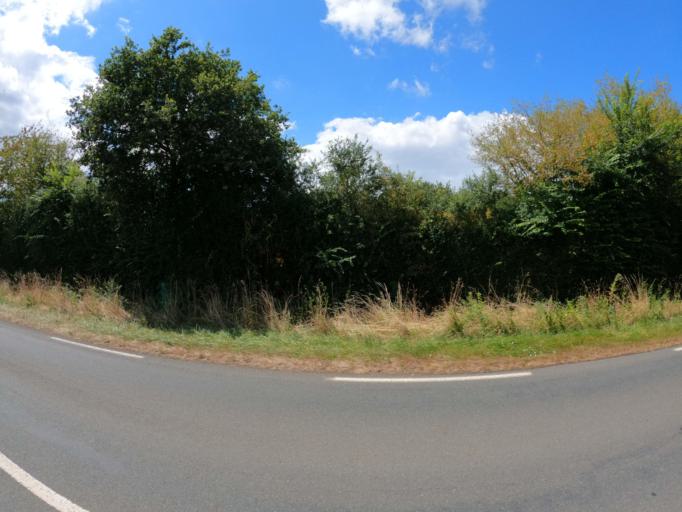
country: FR
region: Pays de la Loire
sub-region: Departement de la Sarthe
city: Brulon
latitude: 47.9253
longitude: -0.2632
